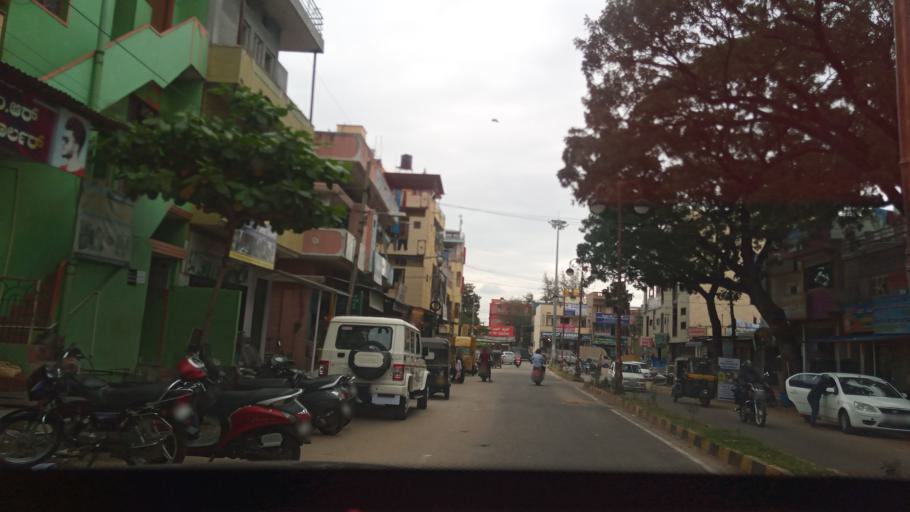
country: IN
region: Karnataka
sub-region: Mysore
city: Mysore
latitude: 12.2971
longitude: 76.6347
